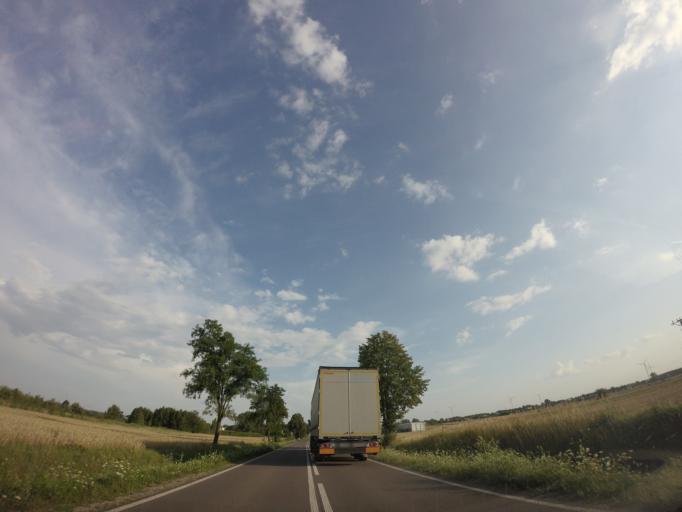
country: PL
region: Lublin Voivodeship
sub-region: Powiat lubartowski
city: Michow
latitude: 51.5329
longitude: 22.3114
